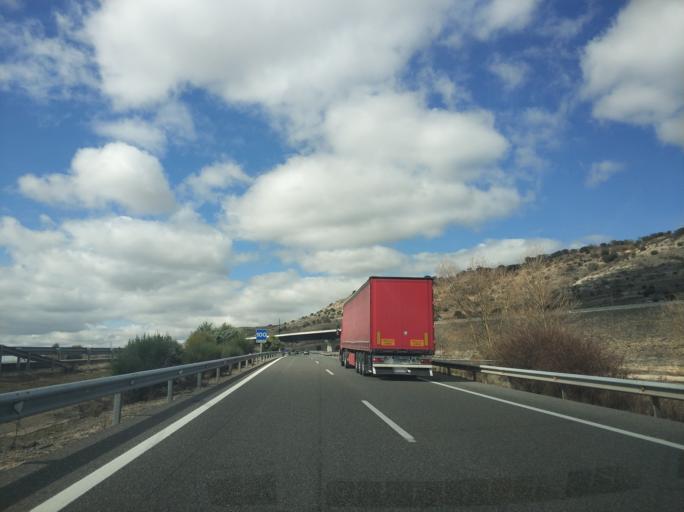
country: ES
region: Castille and Leon
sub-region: Provincia de Palencia
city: Palenzuela
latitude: 42.1173
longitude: -4.1564
